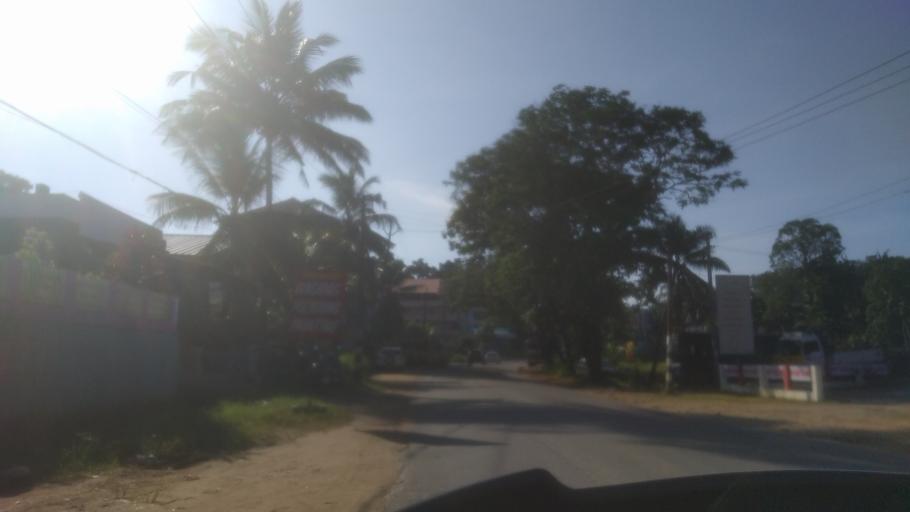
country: IN
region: Kerala
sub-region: Ernakulam
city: Ramamangalam
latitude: 9.9790
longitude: 76.4881
